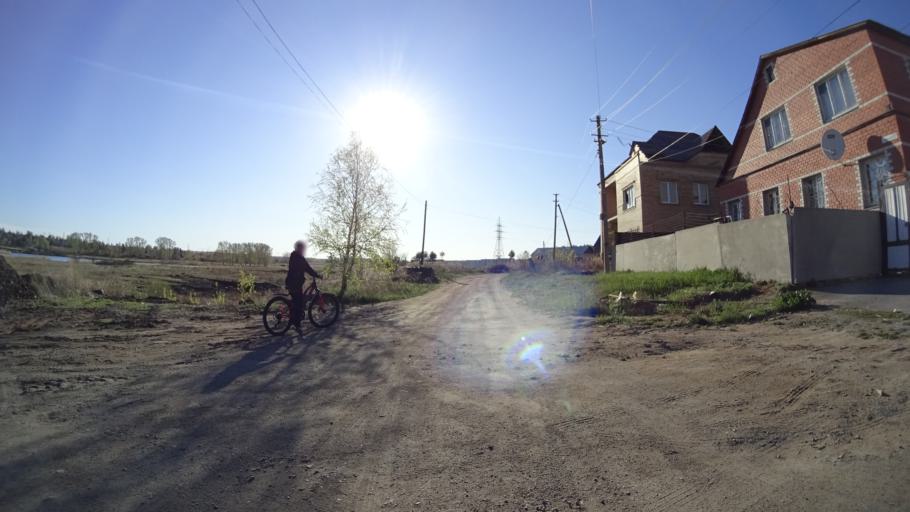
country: RU
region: Chelyabinsk
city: Troitsk
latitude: 54.0689
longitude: 61.5329
